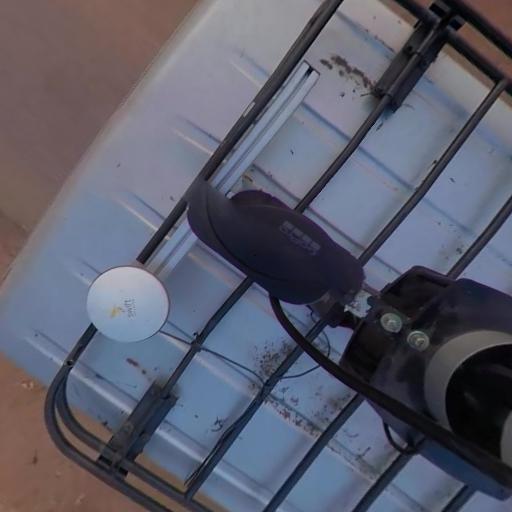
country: IN
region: Telangana
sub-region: Nalgonda
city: Suriapet
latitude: 17.0562
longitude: 79.5491
